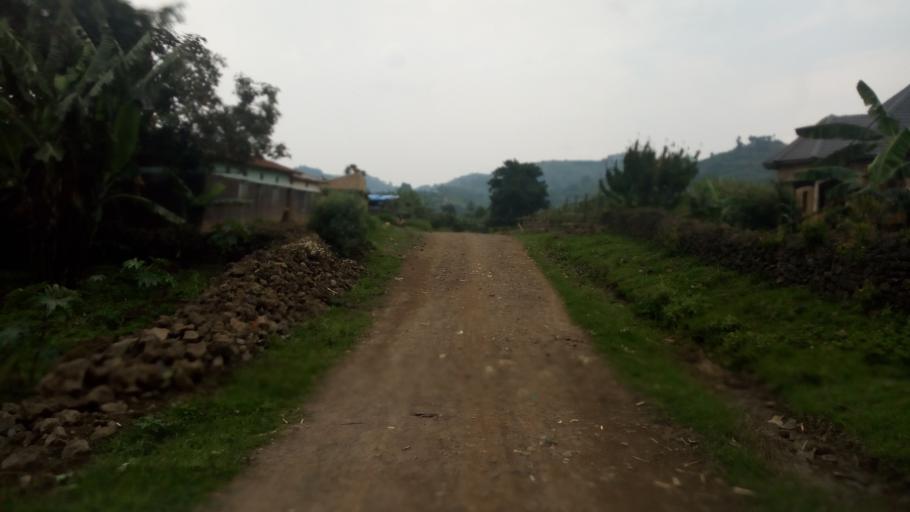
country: UG
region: Western Region
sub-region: Kisoro District
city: Kisoro
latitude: -1.2647
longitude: 29.6264
